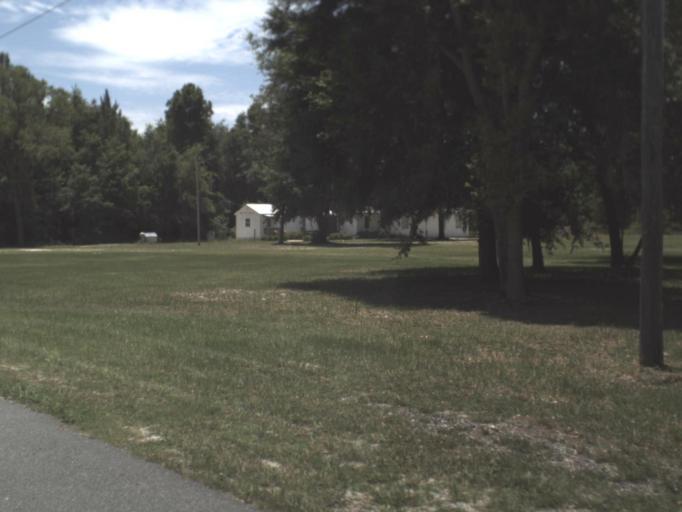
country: US
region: Florida
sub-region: Dixie County
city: Cross City
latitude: 29.7486
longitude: -82.9845
